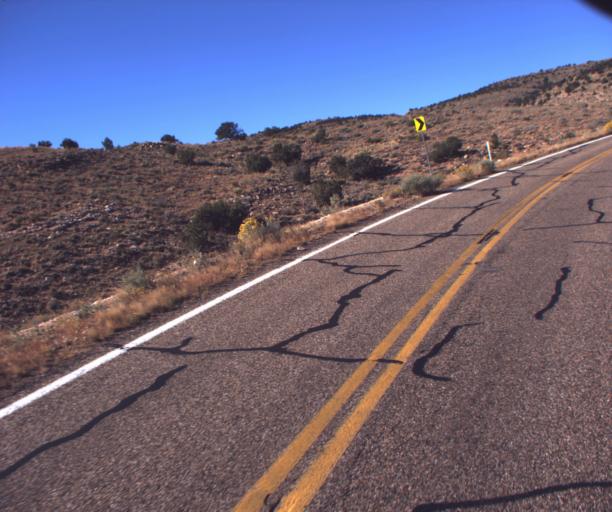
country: US
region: Arizona
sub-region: Coconino County
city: Fredonia
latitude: 36.7314
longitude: -112.0596
